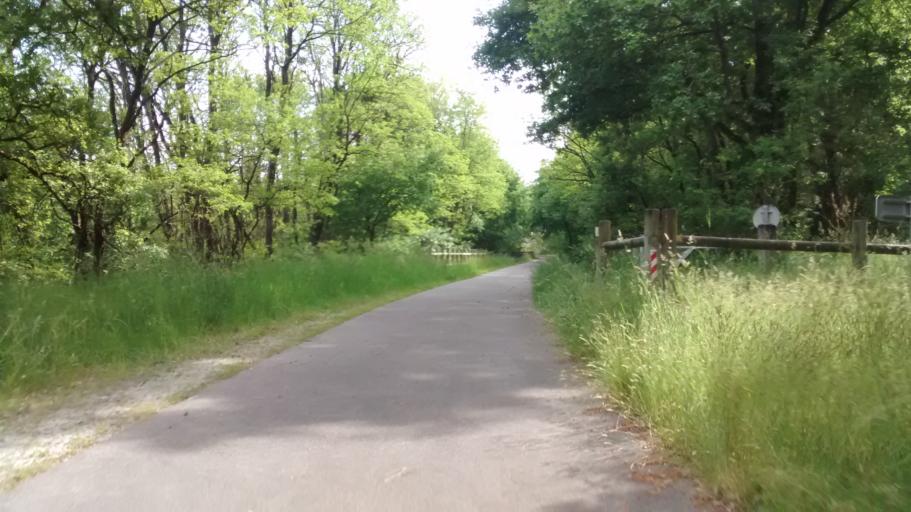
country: FR
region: Brittany
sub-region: Departement du Morbihan
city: Pleucadeuc
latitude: 47.7667
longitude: -2.3953
